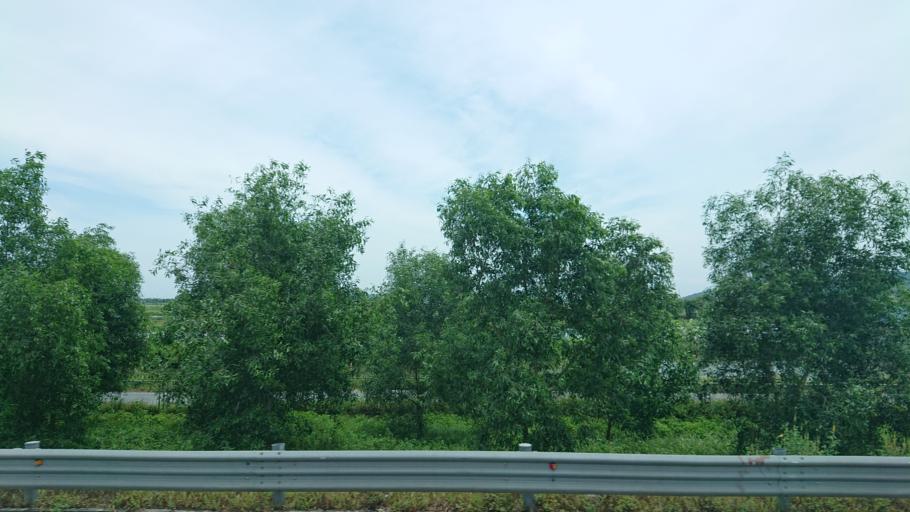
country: VN
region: Hai Phong
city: Tien Lang
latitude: 20.7709
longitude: 106.5953
